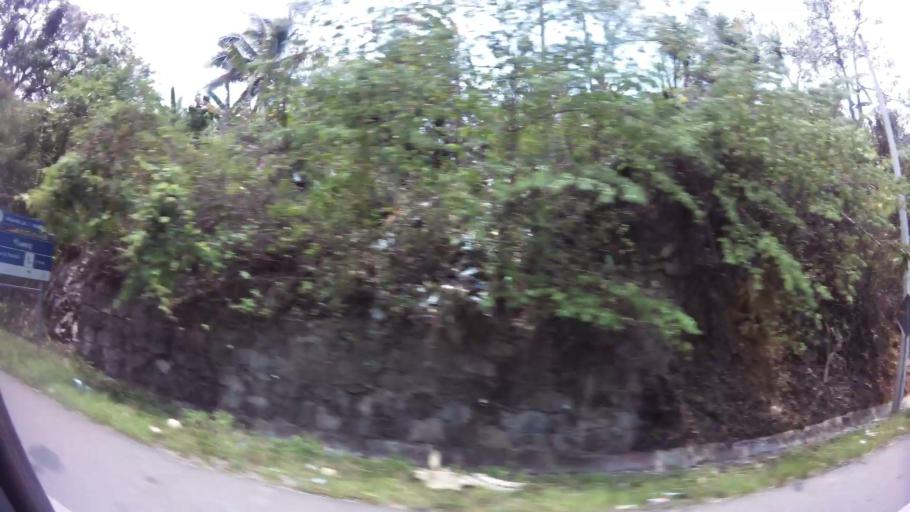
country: HN
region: Comayagua
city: Taulabe
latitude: 14.6874
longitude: -87.9481
